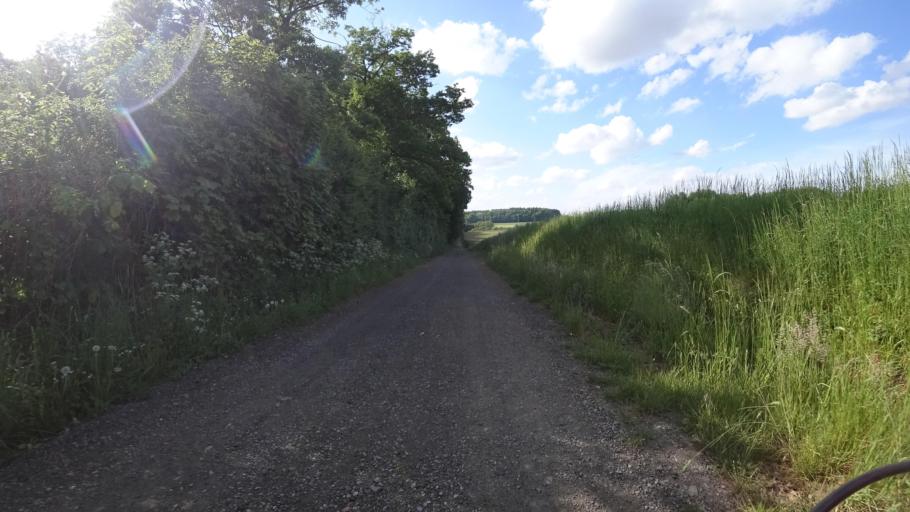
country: BE
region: Wallonia
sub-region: Province de Namur
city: Namur
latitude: 50.4978
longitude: 4.8220
